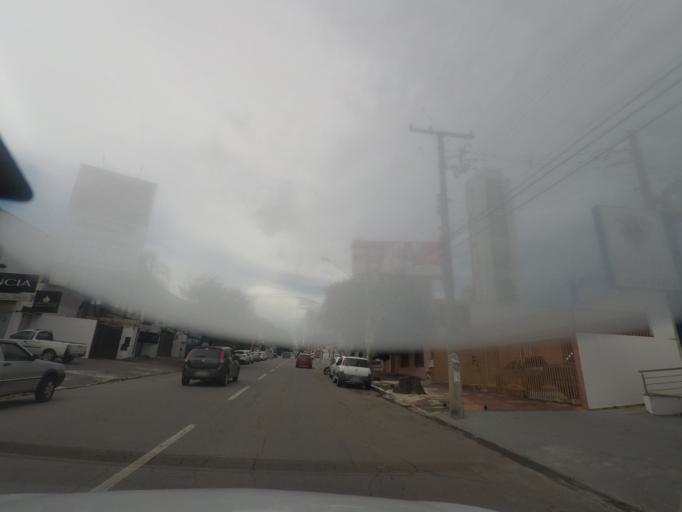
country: BR
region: Goias
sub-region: Goiania
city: Goiania
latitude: -16.6924
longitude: -49.2661
